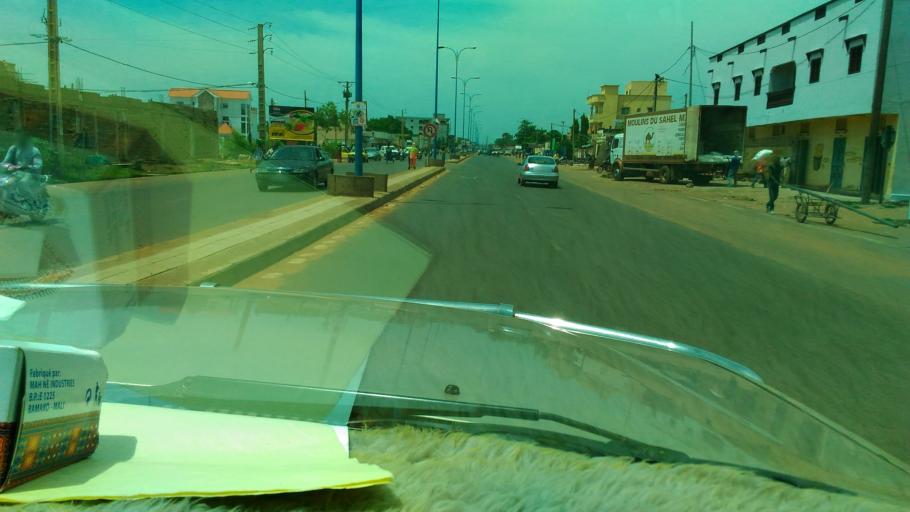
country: ML
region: Bamako
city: Bamako
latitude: 12.6054
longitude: -8.0483
